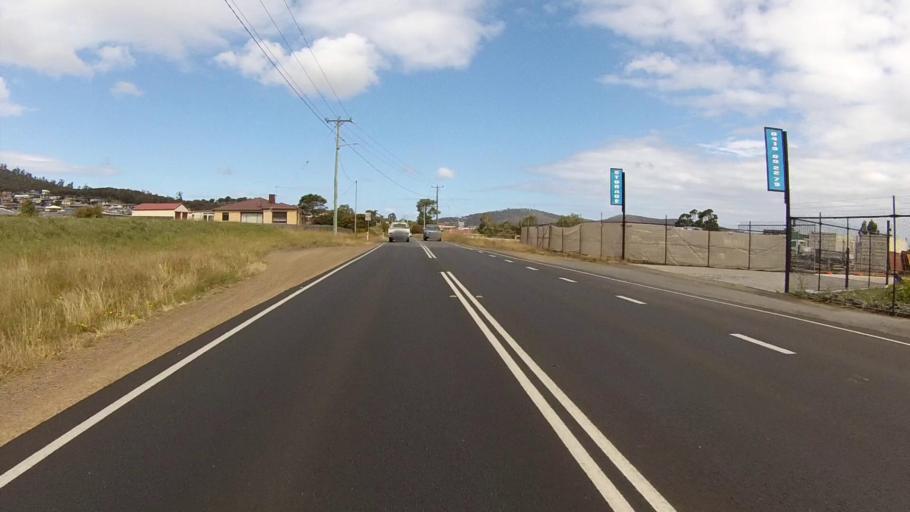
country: AU
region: Tasmania
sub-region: Clarence
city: Rokeby
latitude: -42.9032
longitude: 147.4503
